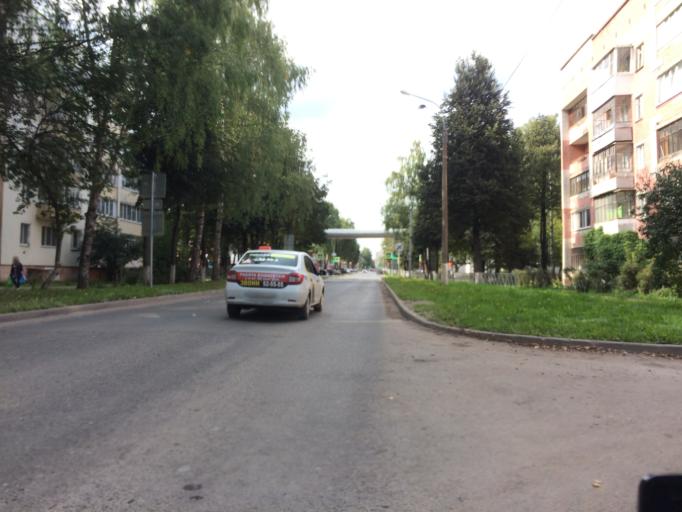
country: RU
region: Mariy-El
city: Yoshkar-Ola
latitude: 56.6309
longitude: 47.8772
